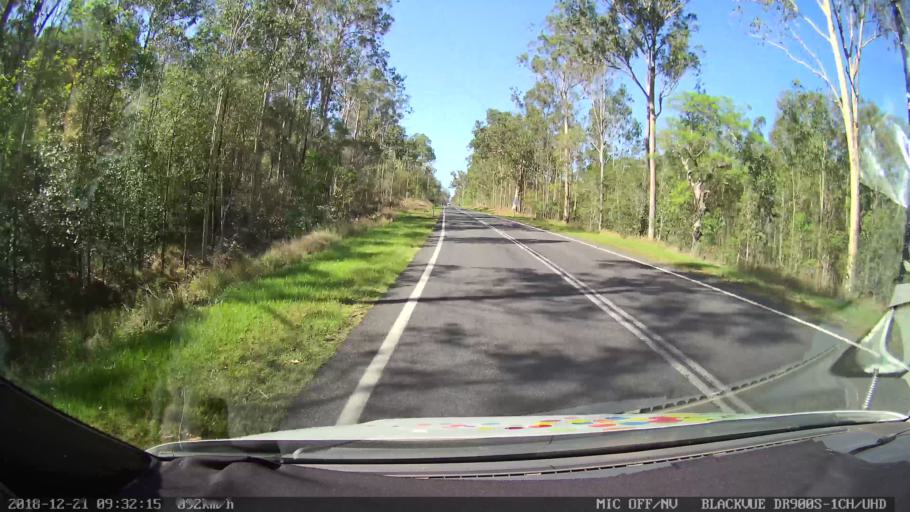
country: AU
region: New South Wales
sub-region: Clarence Valley
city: Maclean
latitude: -29.4679
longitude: 152.9794
